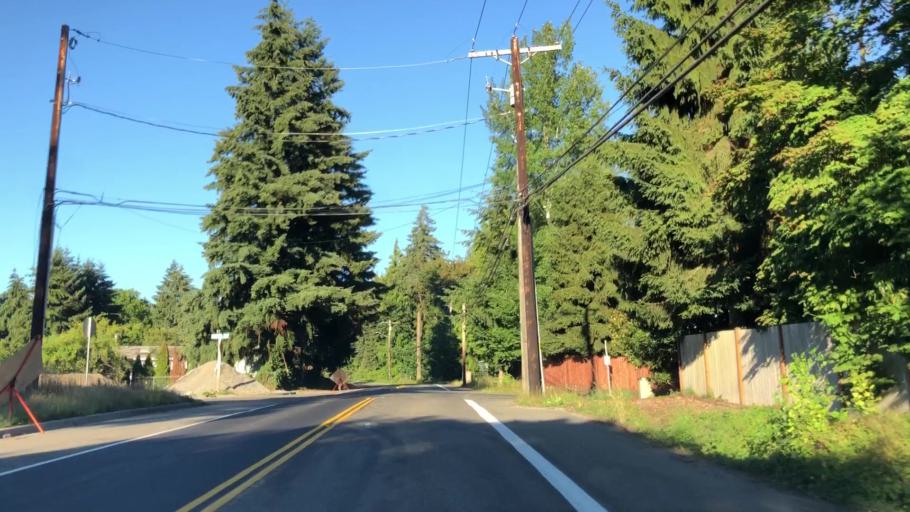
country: US
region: Washington
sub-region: Snohomish County
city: North Creek
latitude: 47.8200
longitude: -122.1953
